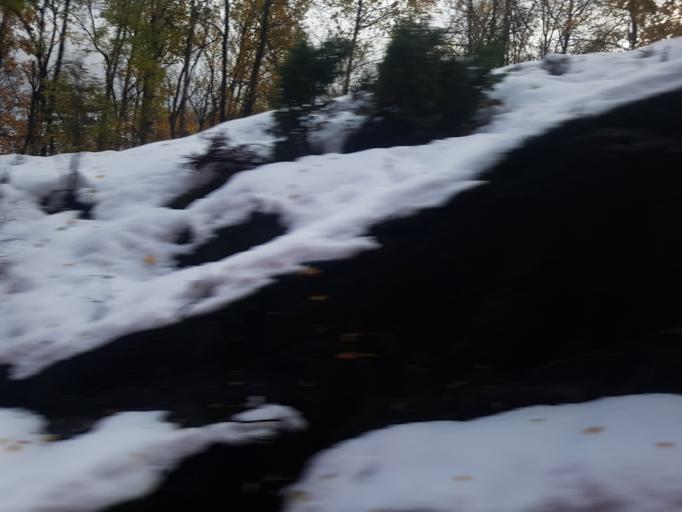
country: NO
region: Sor-Trondelag
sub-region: Oppdal
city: Oppdal
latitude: 62.3462
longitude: 9.6260
